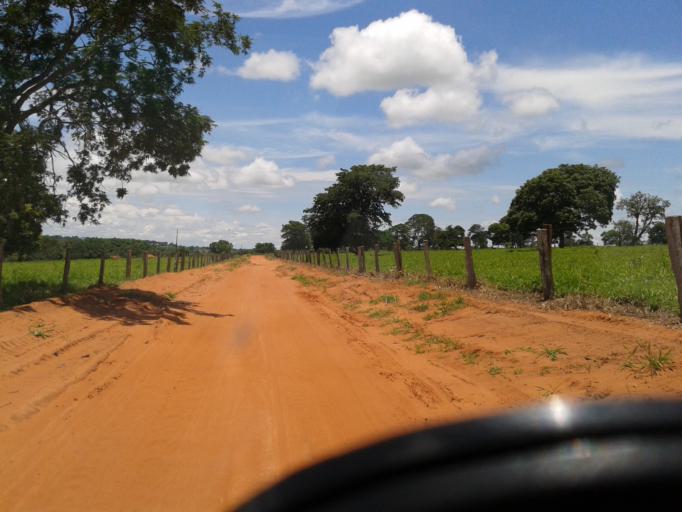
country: BR
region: Minas Gerais
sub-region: Santa Vitoria
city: Santa Vitoria
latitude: -18.9386
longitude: -49.8597
